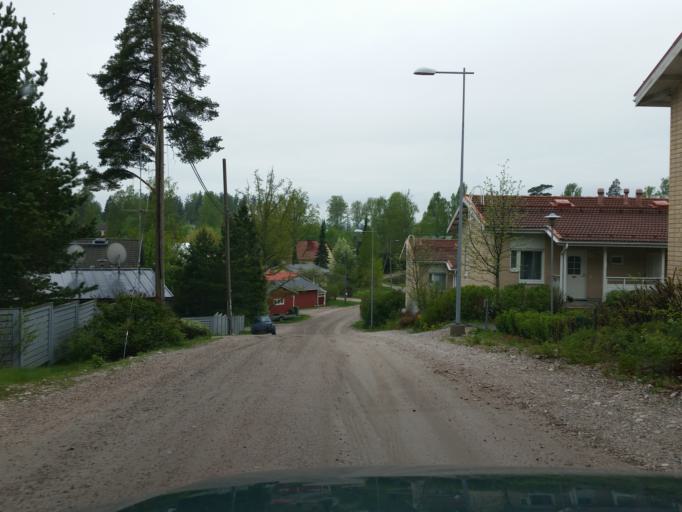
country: FI
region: Uusimaa
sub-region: Helsinki
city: Kilo
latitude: 60.2184
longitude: 24.7721
